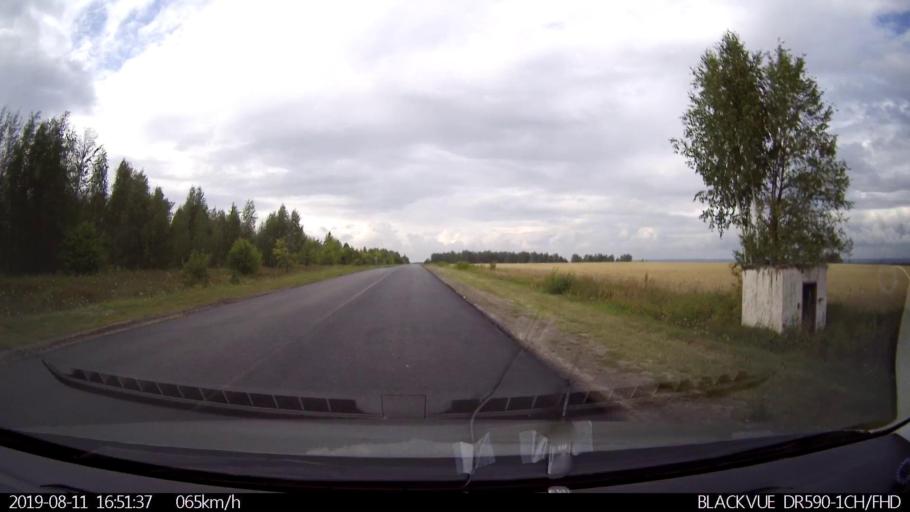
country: RU
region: Ulyanovsk
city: Mayna
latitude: 54.2390
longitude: 47.6764
